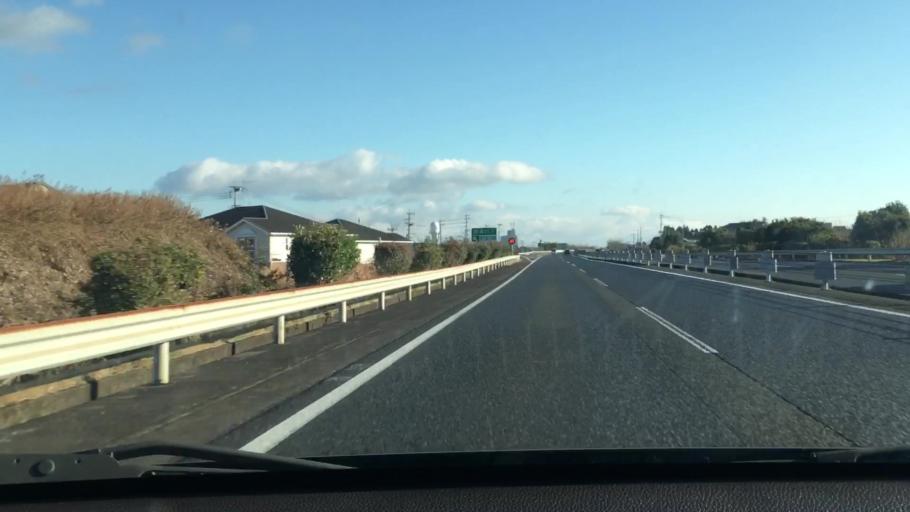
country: JP
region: Kagoshima
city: Kajiki
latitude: 31.8027
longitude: 130.7111
